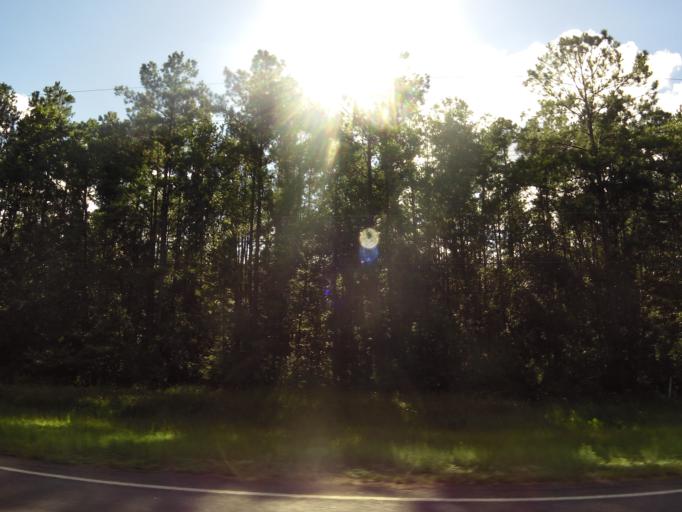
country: US
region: Georgia
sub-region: Camden County
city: Woodbine
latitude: 30.9932
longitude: -81.7300
